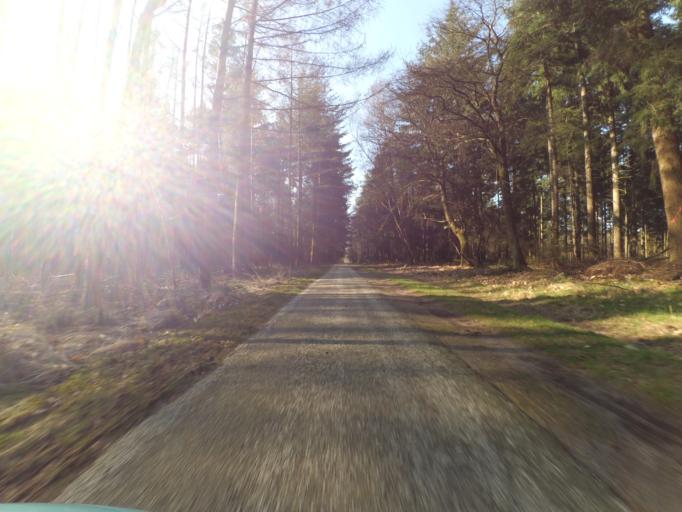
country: NL
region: Gelderland
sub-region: Gemeente Arnhem
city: Hoogkamp
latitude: 52.0487
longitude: 5.8531
